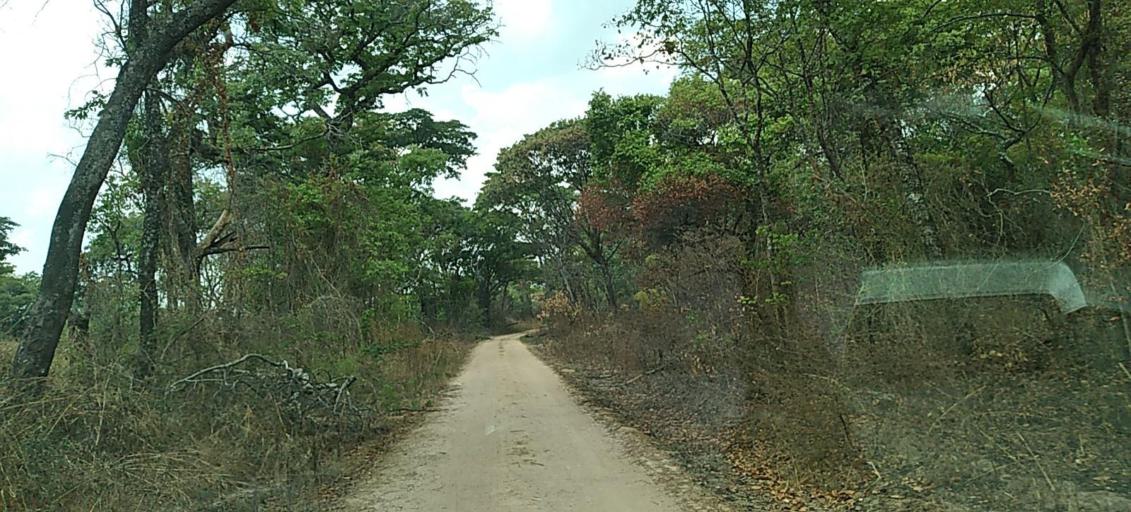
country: ZM
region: Copperbelt
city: Chingola
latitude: -12.7550
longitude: 27.7094
